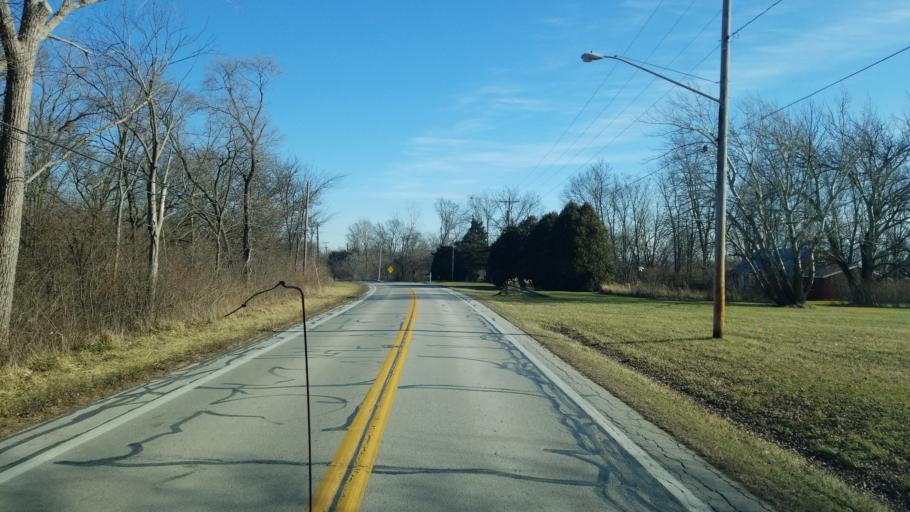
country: US
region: Ohio
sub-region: Wood County
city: Weston
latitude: 41.4096
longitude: -83.8802
